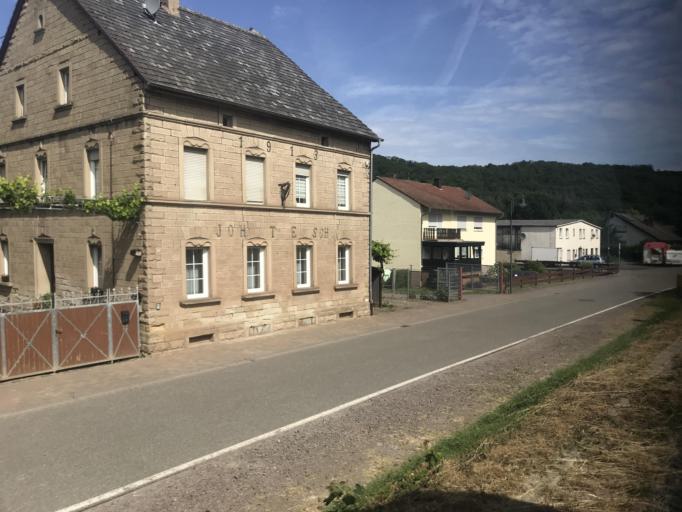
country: DE
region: Rheinland-Pfalz
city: Boos
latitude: 49.7936
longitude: 7.7192
